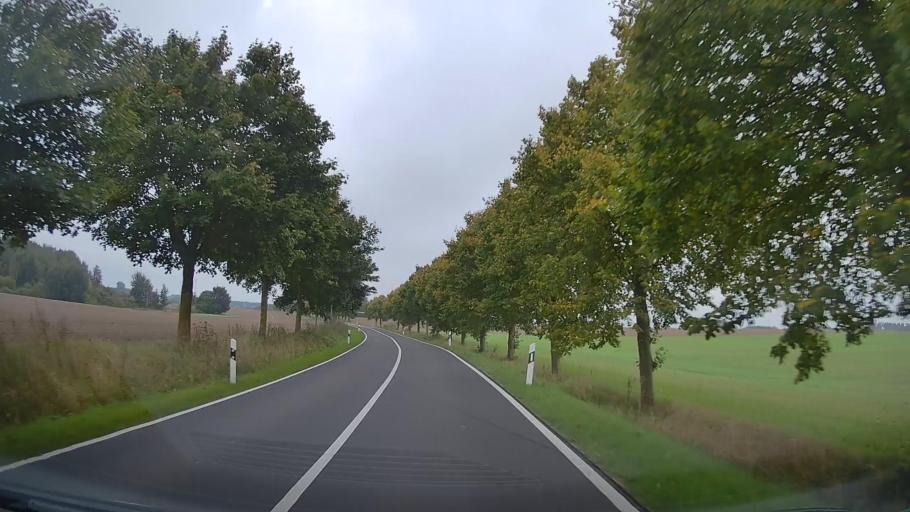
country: DE
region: Mecklenburg-Vorpommern
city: Schwaan
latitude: 53.8949
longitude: 12.1939
